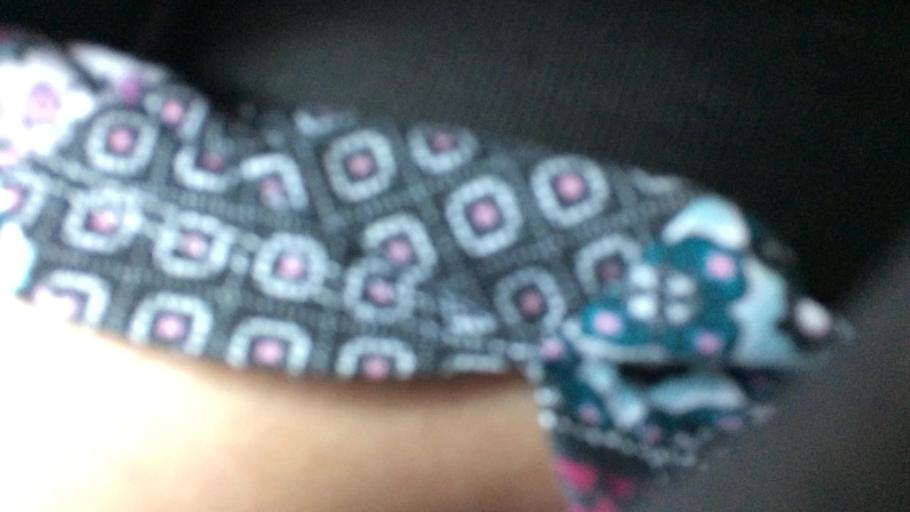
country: US
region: New Mexico
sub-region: Colfax County
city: Springer
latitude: 36.2419
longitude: -104.6505
